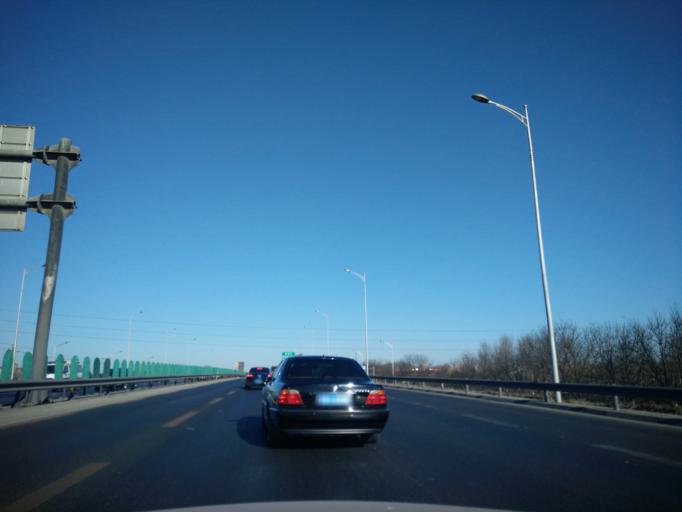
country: CN
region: Beijing
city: Xihongmen
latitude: 39.8110
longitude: 116.3391
